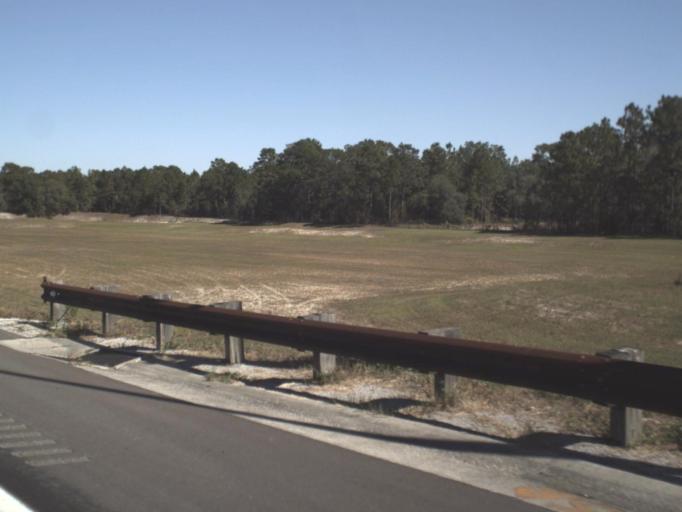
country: US
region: Florida
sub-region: Hernando County
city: Brookridge
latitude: 28.5272
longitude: -82.4792
